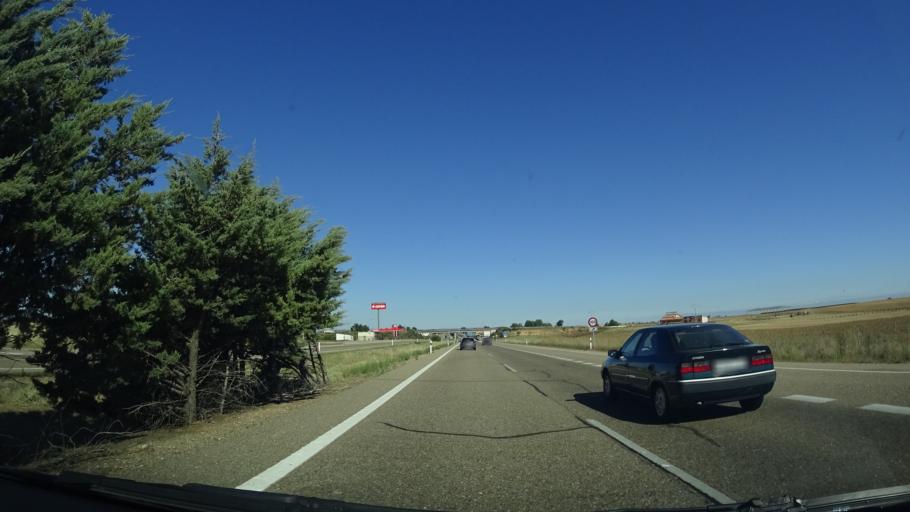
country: ES
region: Castille and Leon
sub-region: Provincia de Zamora
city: San Esteban del Molar
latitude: 41.9352
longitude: -5.5419
